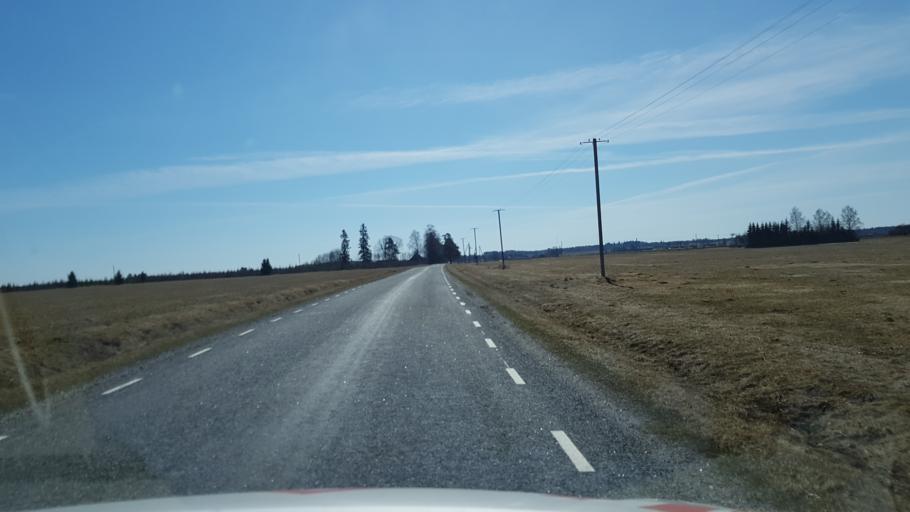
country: EE
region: Laeaene-Virumaa
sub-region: Vinni vald
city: Vinni
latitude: 59.1223
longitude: 26.5221
